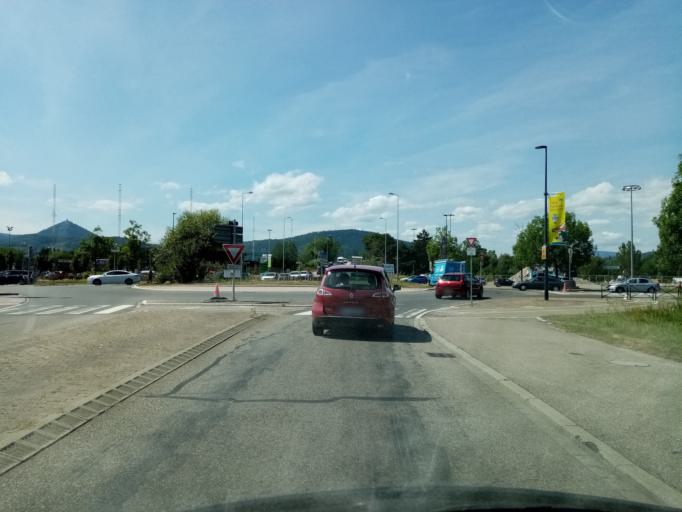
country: FR
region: Alsace
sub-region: Departement du Bas-Rhin
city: Selestat
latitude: 48.2492
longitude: 7.4375
